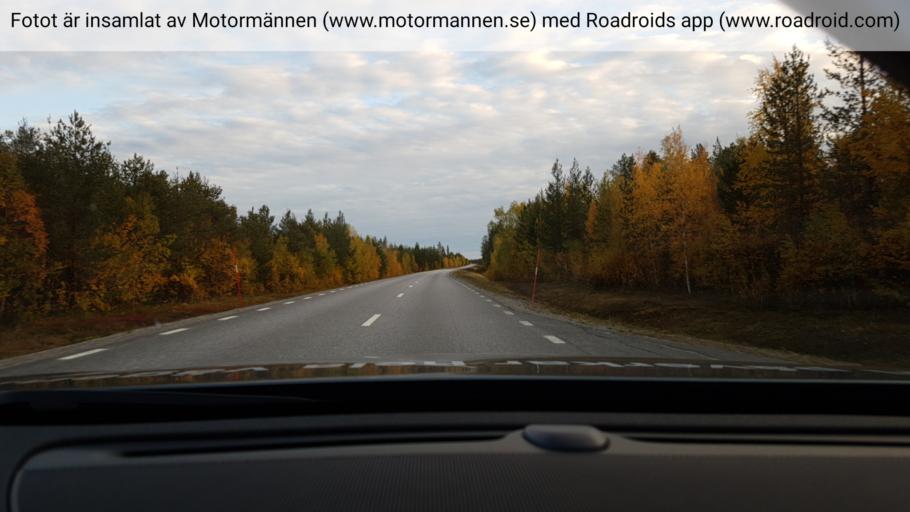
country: SE
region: Norrbotten
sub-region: Jokkmokks Kommun
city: Jokkmokk
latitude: 66.4170
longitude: 19.6869
